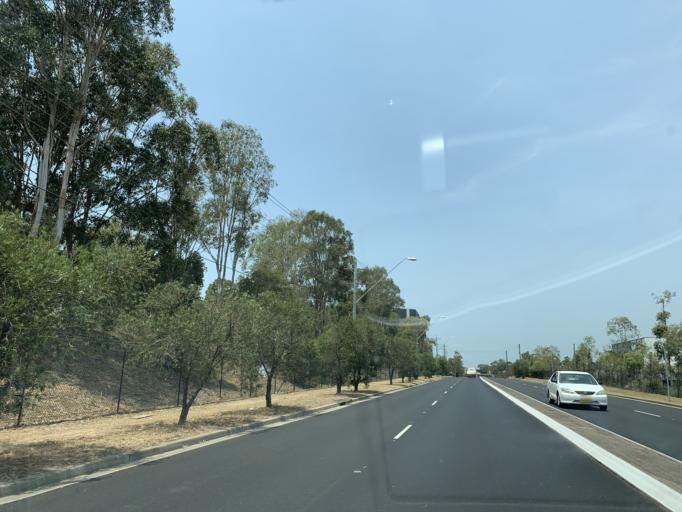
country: AU
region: New South Wales
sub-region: Blacktown
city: Doonside
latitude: -33.7971
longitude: 150.8708
